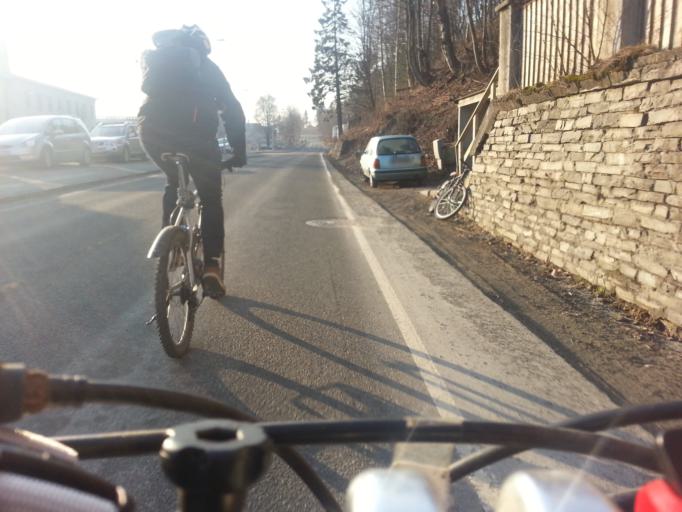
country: NO
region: Sor-Trondelag
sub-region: Trondheim
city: Trondheim
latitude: 63.4207
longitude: 10.3766
